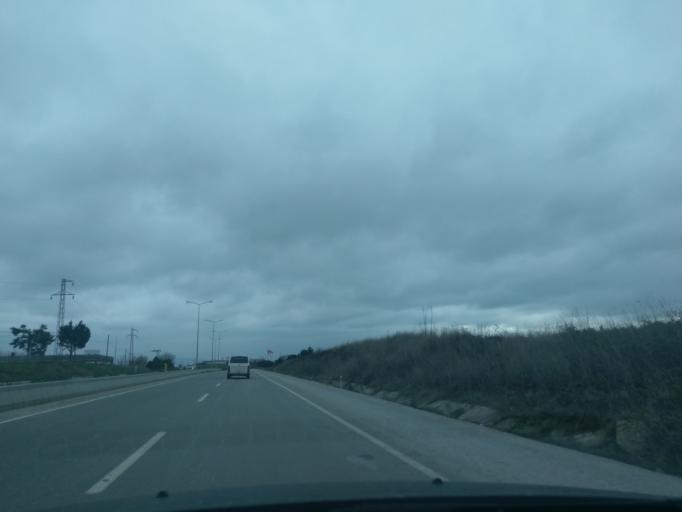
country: TR
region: Istanbul
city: Muratbey
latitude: 41.1176
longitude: 28.4963
